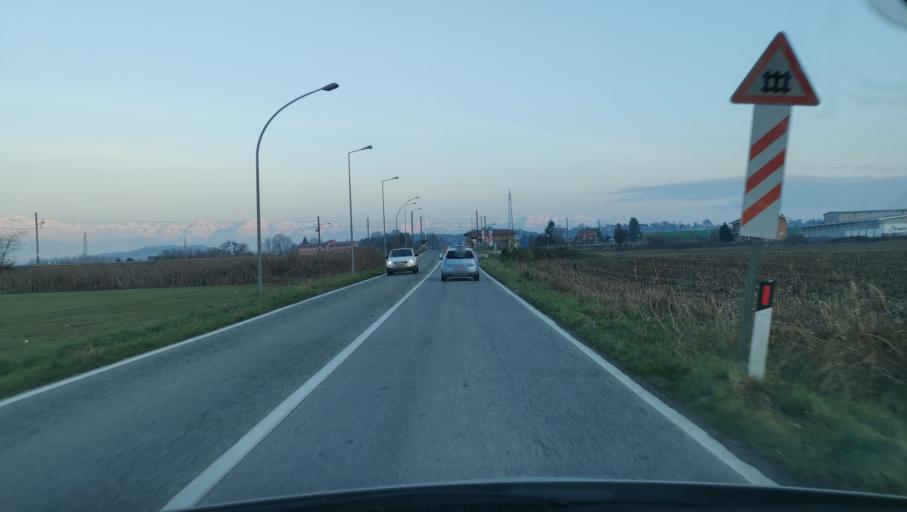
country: IT
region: Piedmont
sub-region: Provincia di Torino
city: Caluso
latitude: 45.2906
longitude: 7.8918
